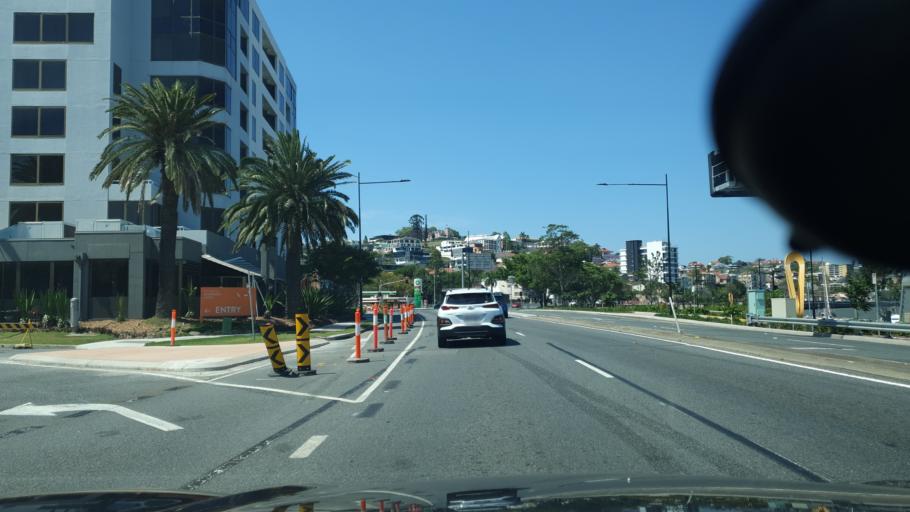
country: AU
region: Queensland
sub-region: Brisbane
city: Ascot
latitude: -27.4410
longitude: 153.0480
